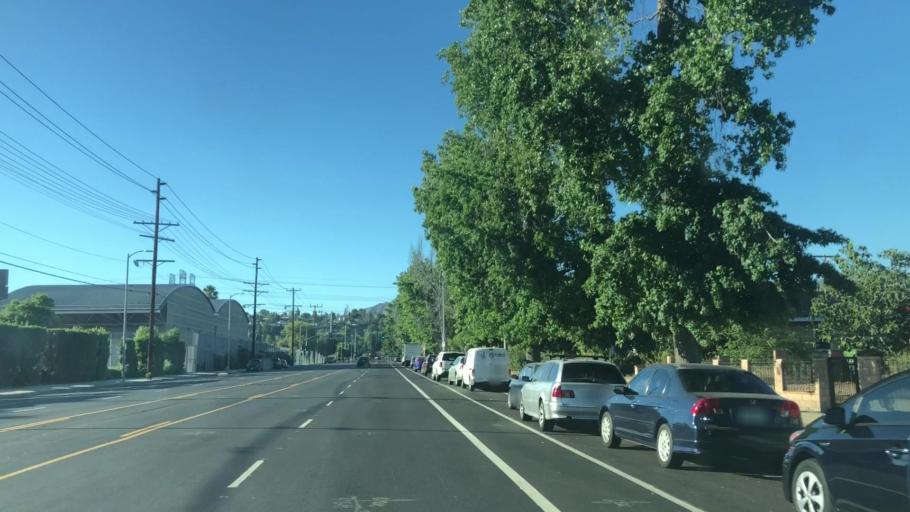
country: US
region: California
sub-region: Los Angeles County
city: San Fernando
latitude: 34.2737
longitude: -118.4846
